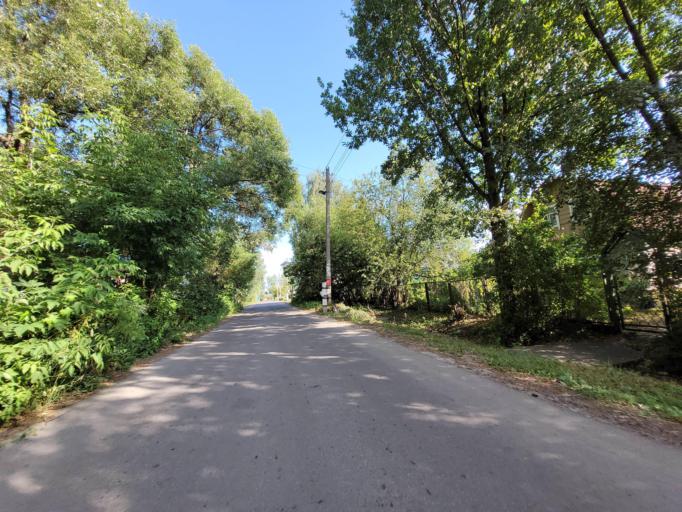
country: RU
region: Moskovskaya
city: Konobeyevo
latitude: 55.4098
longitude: 38.6992
